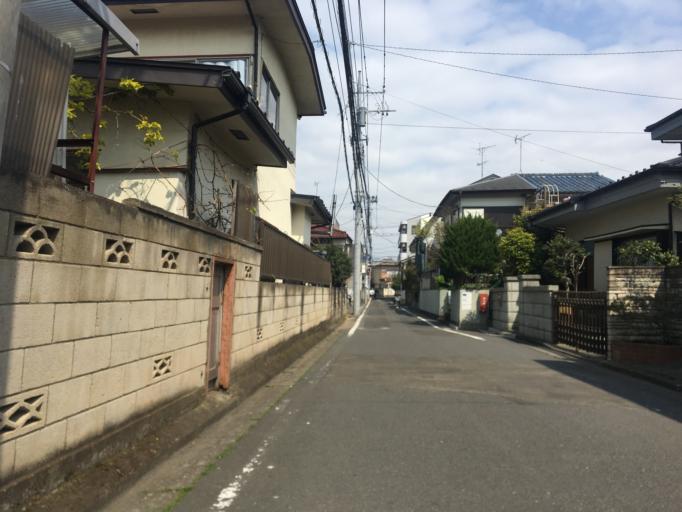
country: JP
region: Saitama
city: Kamifukuoka
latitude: 35.8715
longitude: 139.5172
